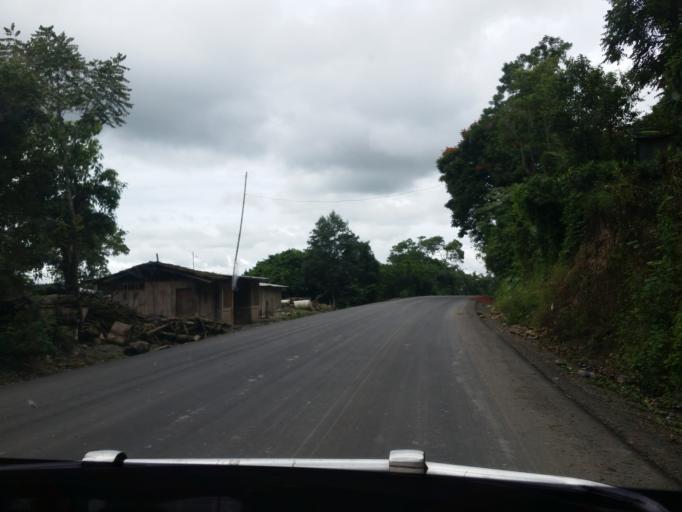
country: NI
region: Jinotega
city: Jinotega
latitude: 13.1604
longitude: -85.9260
